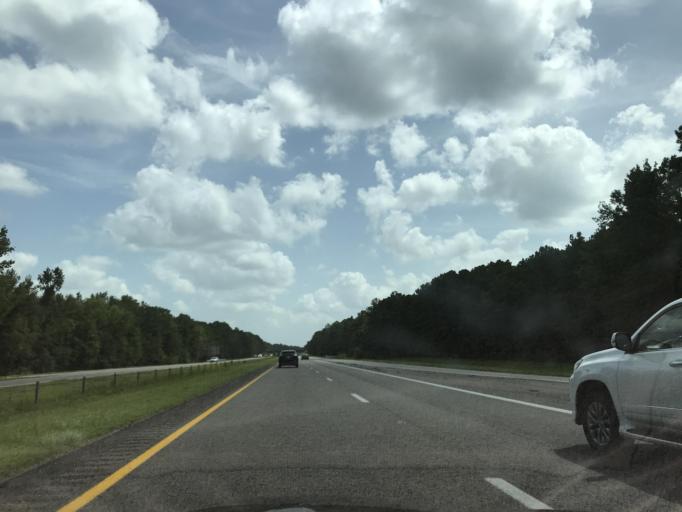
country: US
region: North Carolina
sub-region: Pender County
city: Burgaw
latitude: 34.5737
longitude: -77.9011
